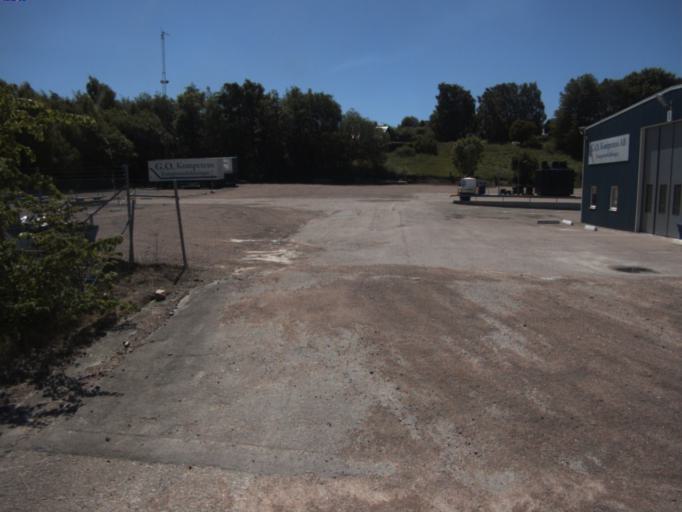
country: SE
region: Skane
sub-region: Helsingborg
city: Glumslov
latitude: 55.9647
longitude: 12.8562
